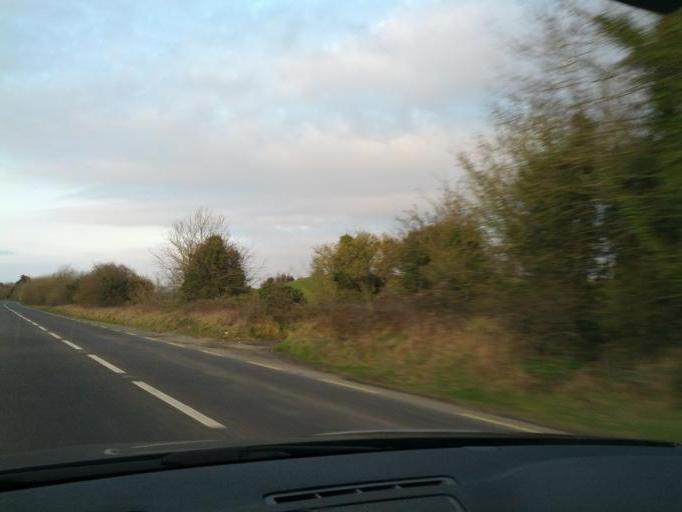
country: IE
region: Munster
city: Nenagh Bridge
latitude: 52.8884
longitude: -8.1915
